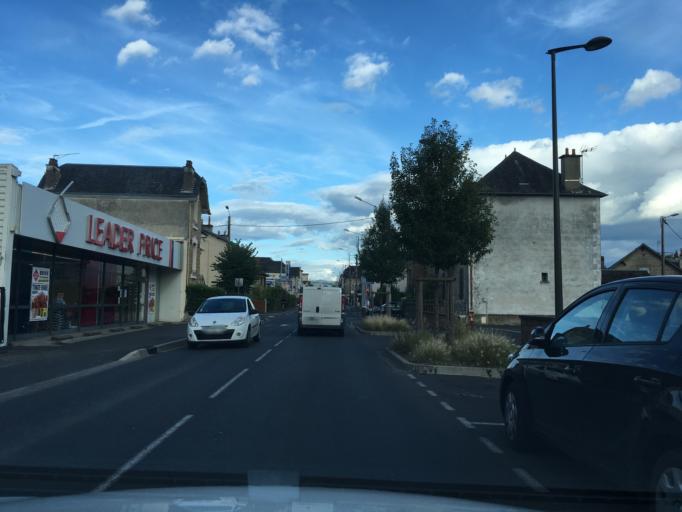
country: FR
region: Limousin
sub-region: Departement de la Correze
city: Brive-la-Gaillarde
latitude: 45.1578
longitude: 1.5487
